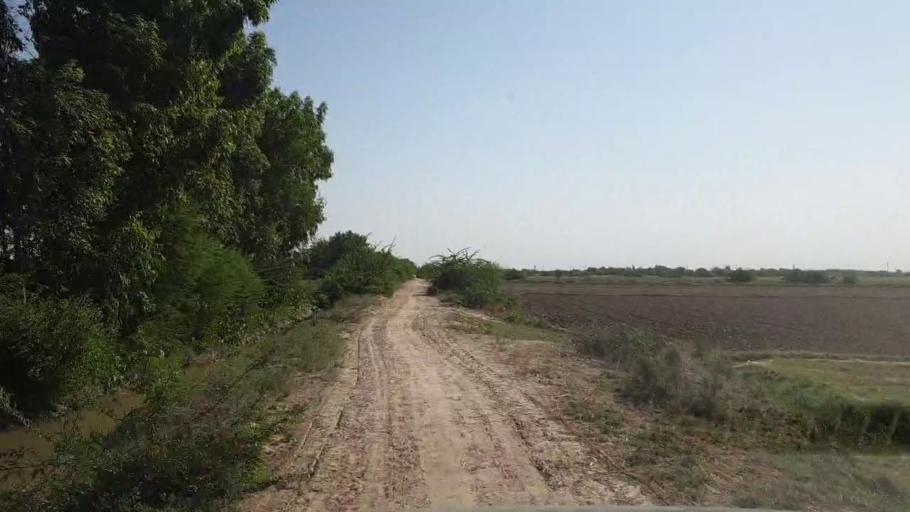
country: PK
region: Sindh
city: Kadhan
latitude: 24.5908
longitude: 69.0081
